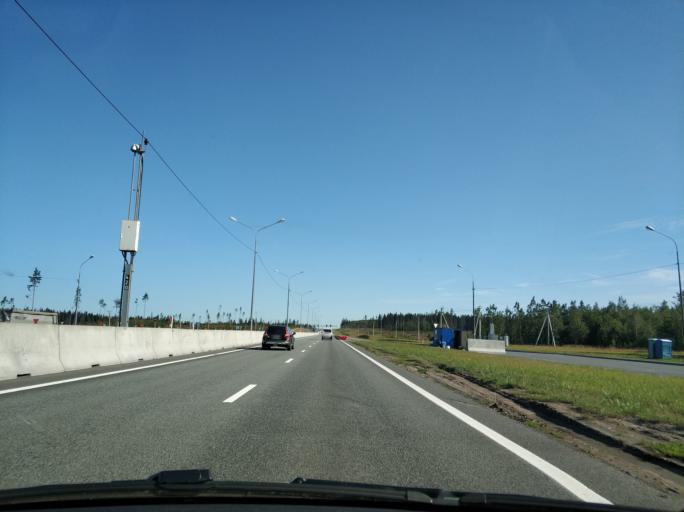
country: RU
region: Leningrad
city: Sosnovo
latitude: 60.4755
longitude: 30.1960
